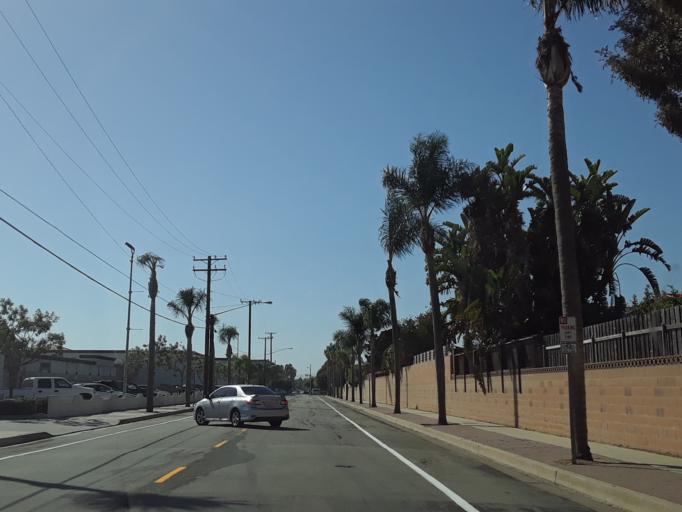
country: US
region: California
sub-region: Orange County
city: Seal Beach
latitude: 33.7451
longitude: -118.0997
